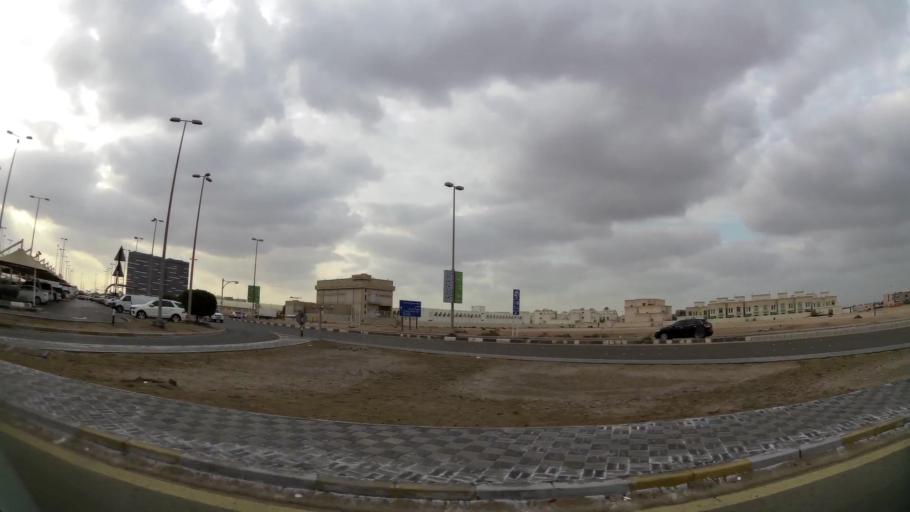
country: AE
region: Abu Dhabi
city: Abu Dhabi
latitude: 24.3740
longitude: 54.5395
